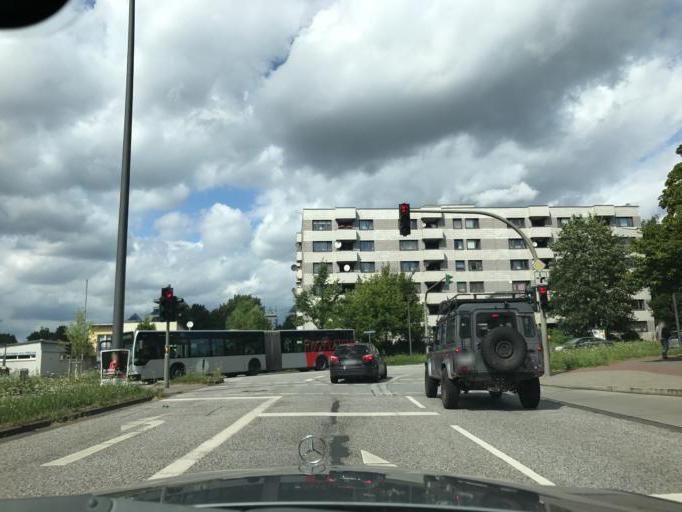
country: DE
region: Hamburg
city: Bergedorf
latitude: 53.5034
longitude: 10.2105
